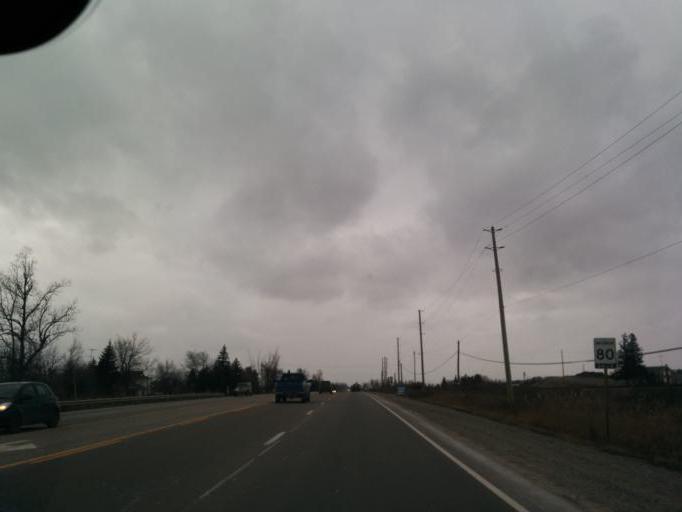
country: CA
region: Ontario
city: Brampton
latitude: 43.7459
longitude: -79.8414
